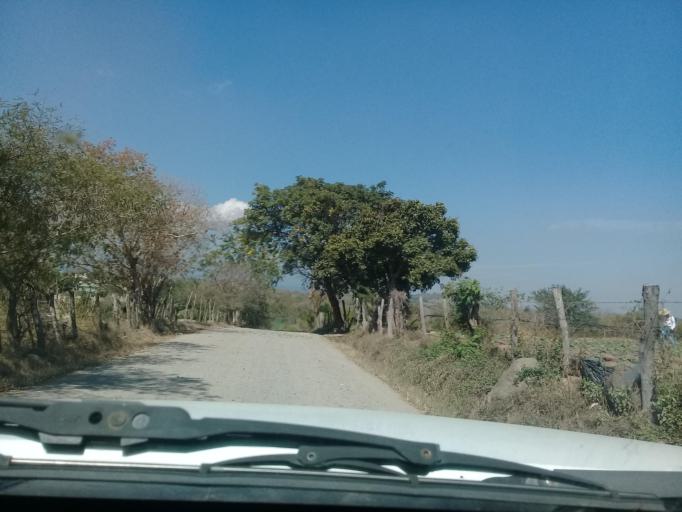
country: MX
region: Veracruz
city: Actopan
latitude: 19.4749
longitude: -96.6409
